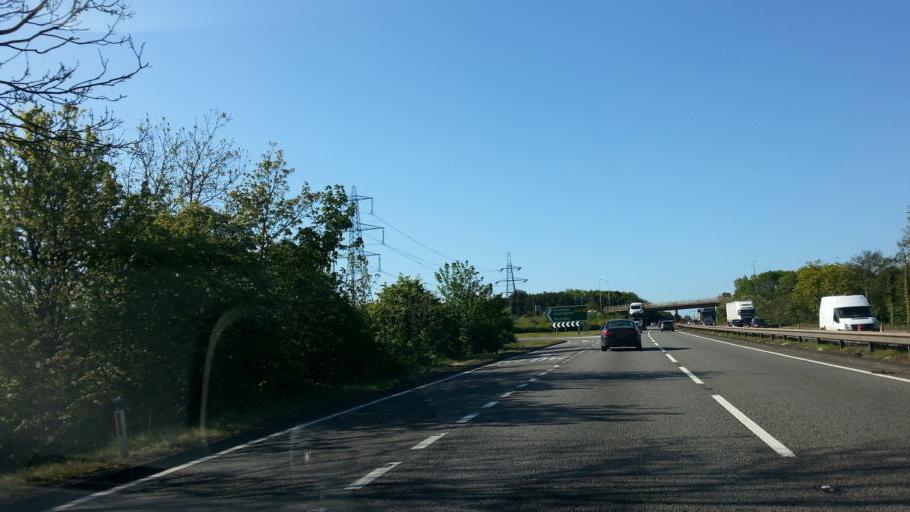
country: GB
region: England
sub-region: Lincolnshire
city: Barrowby
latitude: 52.9164
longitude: -0.6802
